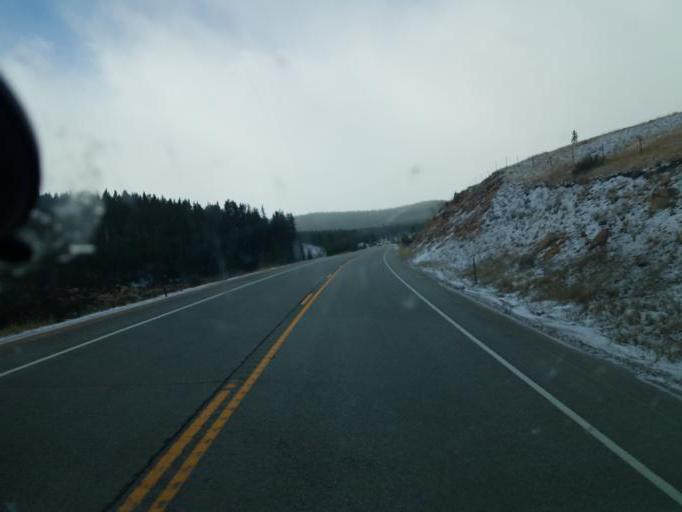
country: US
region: Colorado
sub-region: Clear Creek County
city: Georgetown
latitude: 39.4358
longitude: -105.7549
